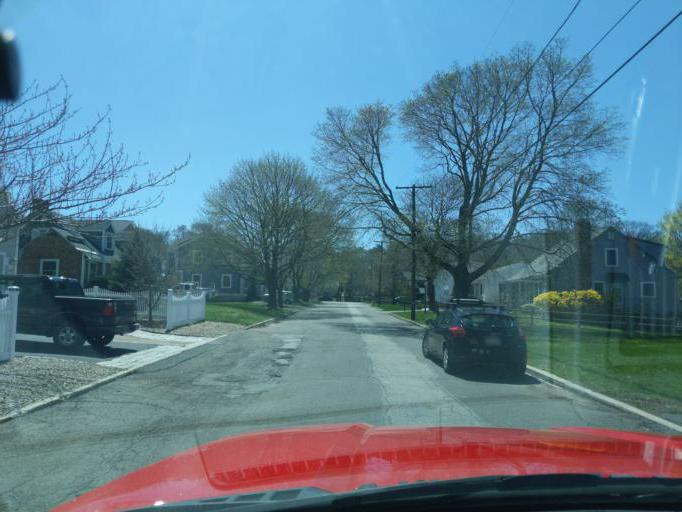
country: US
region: Massachusetts
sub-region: Essex County
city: Rockport
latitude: 42.6556
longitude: -70.6062
